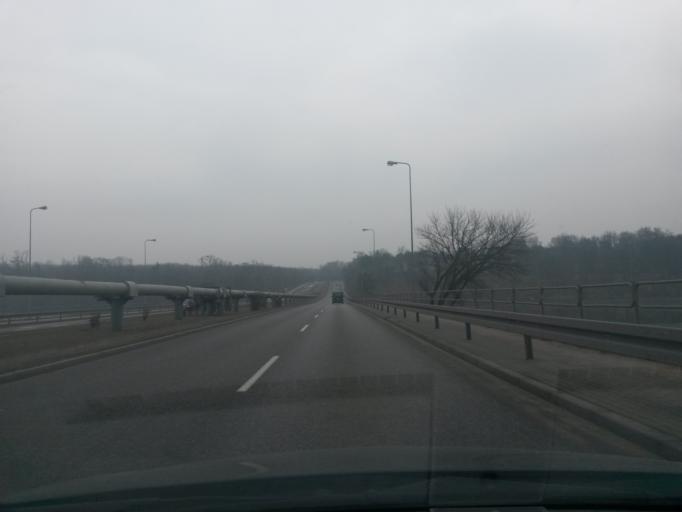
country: PL
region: Masovian Voivodeship
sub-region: Powiat legionowski
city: Nieporet
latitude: 52.4605
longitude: 21.0196
